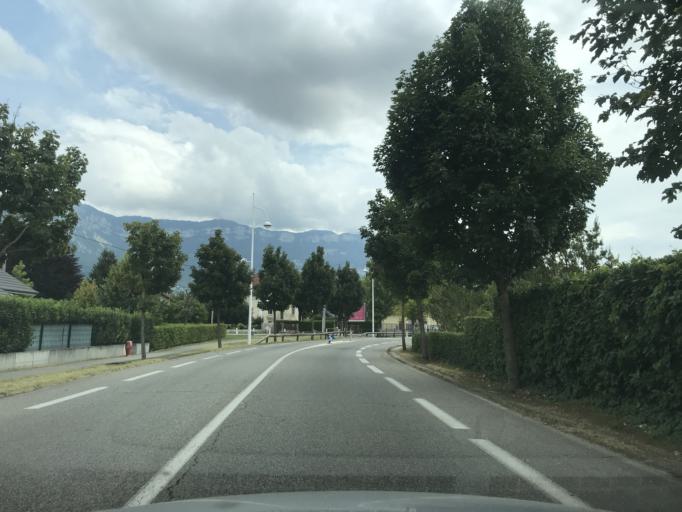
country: FR
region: Rhone-Alpes
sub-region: Departement de la Savoie
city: Tresserve
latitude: 45.6974
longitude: 5.8949
